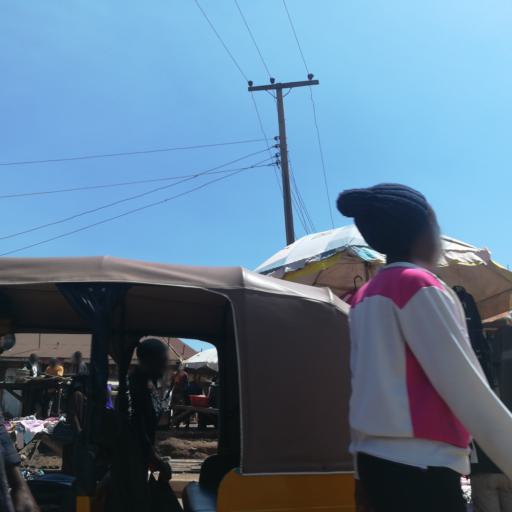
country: NG
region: Plateau
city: Bukuru
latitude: 9.7913
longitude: 8.8647
